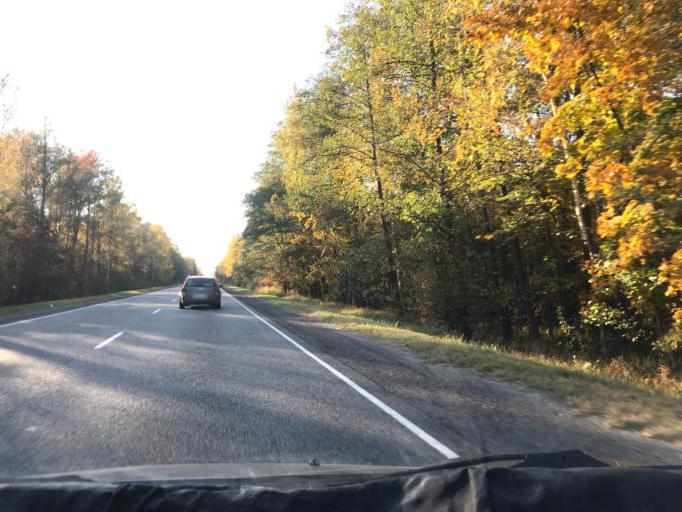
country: BY
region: Gomel
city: Zhytkavichy
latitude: 52.2741
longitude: 28.1465
